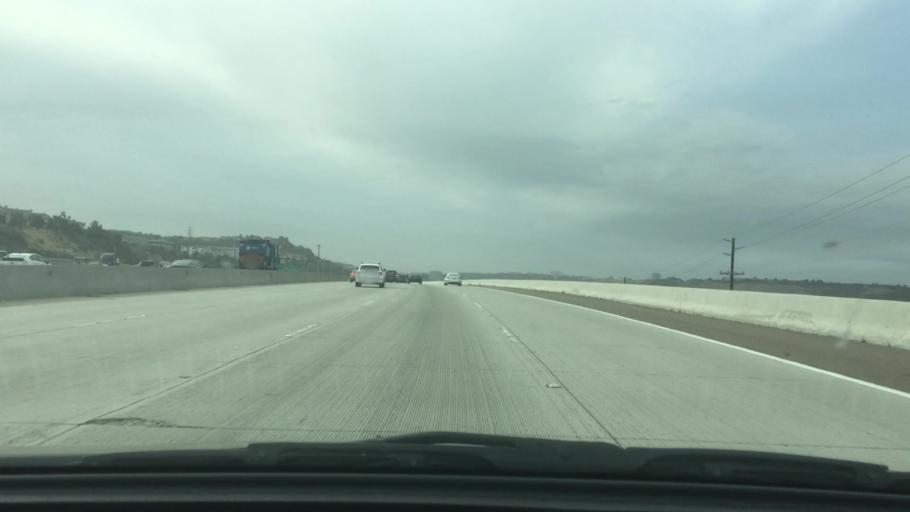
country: US
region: California
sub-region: San Diego County
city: Del Mar
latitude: 32.9193
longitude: -117.2367
